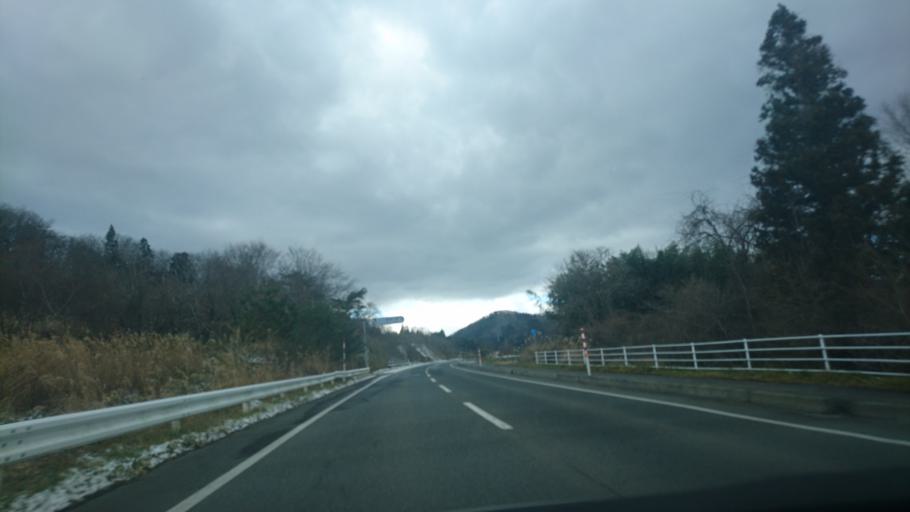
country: JP
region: Iwate
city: Mizusawa
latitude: 39.1796
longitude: 141.3090
